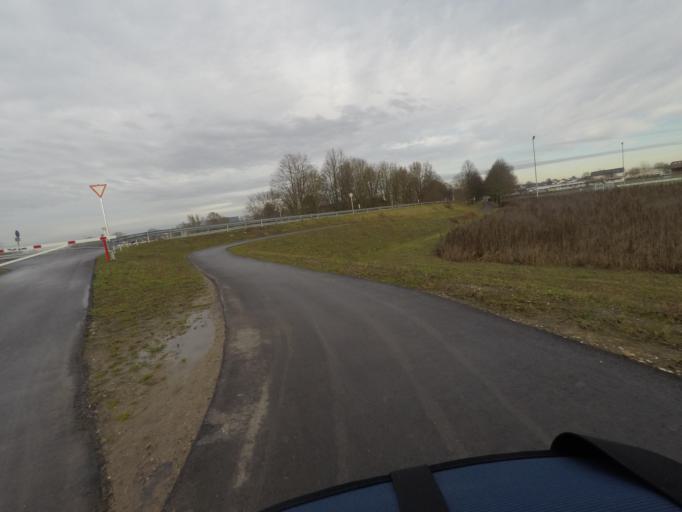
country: DE
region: Baden-Wuerttemberg
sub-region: Karlsruhe Region
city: Steinmauern
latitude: 48.8906
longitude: 8.1924
